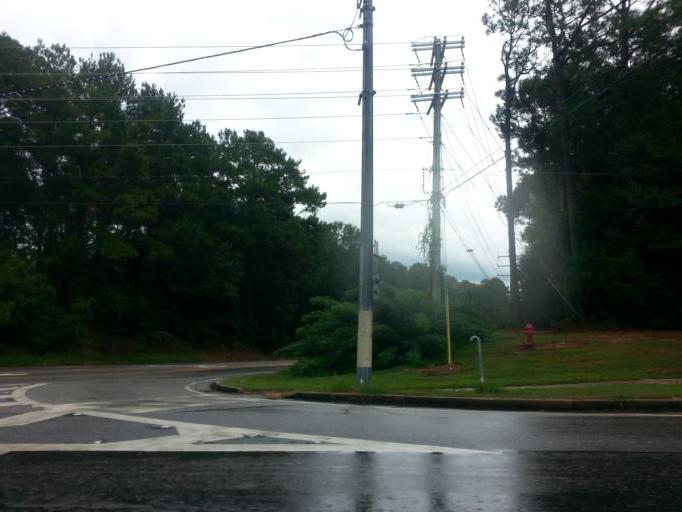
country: US
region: Alabama
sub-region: Baldwin County
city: Fairhope
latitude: 30.5454
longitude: -87.8888
